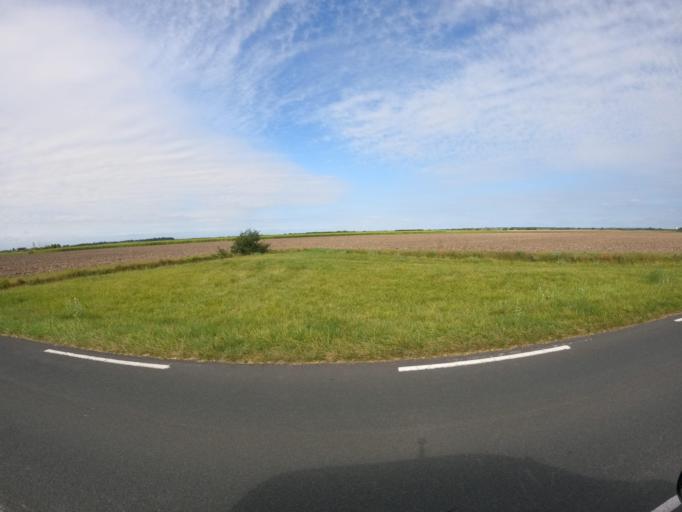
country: FR
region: Pays de la Loire
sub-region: Departement de la Vendee
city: Triaize
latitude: 46.3814
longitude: -1.2026
